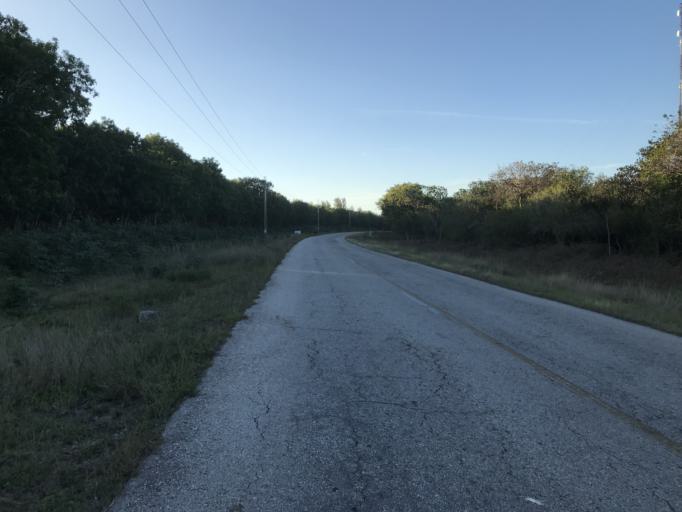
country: CU
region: Cienfuegos
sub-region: Municipio de Aguada de Pasajeros
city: Aguada de Pasajeros
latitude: 22.0690
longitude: -81.0513
